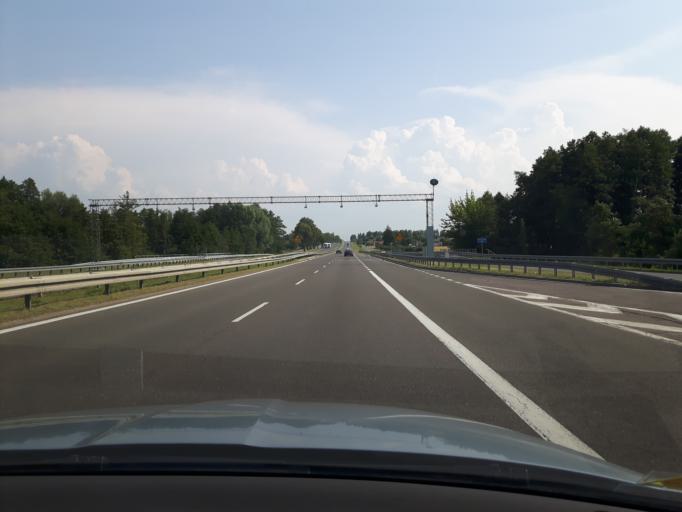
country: PL
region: Masovian Voivodeship
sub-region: Powiat plonski
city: Zaluski
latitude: 52.5670
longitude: 20.4877
